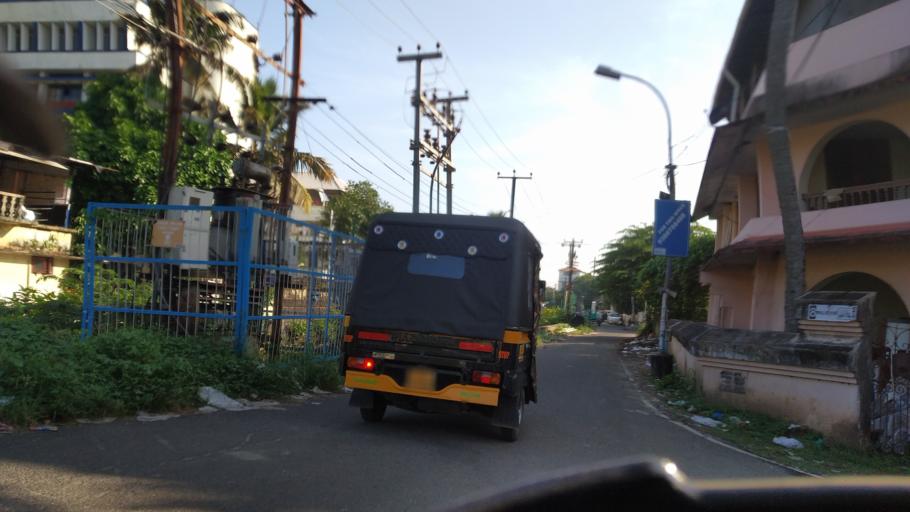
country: IN
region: Kerala
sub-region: Ernakulam
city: Cochin
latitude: 9.9880
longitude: 76.2913
